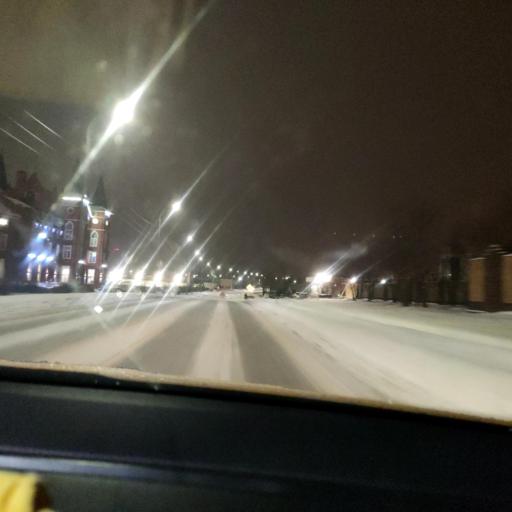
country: RU
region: Moskovskaya
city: Rozhdestveno
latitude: 55.8085
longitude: 36.9750
